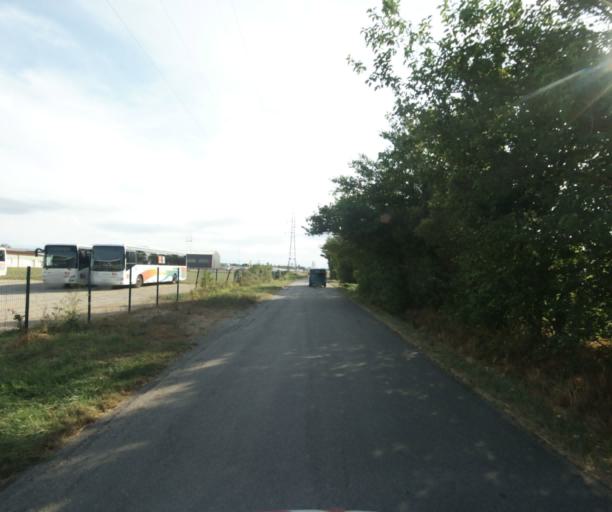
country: FR
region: Midi-Pyrenees
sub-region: Departement de la Haute-Garonne
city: Revel
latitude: 43.4583
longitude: 1.9773
